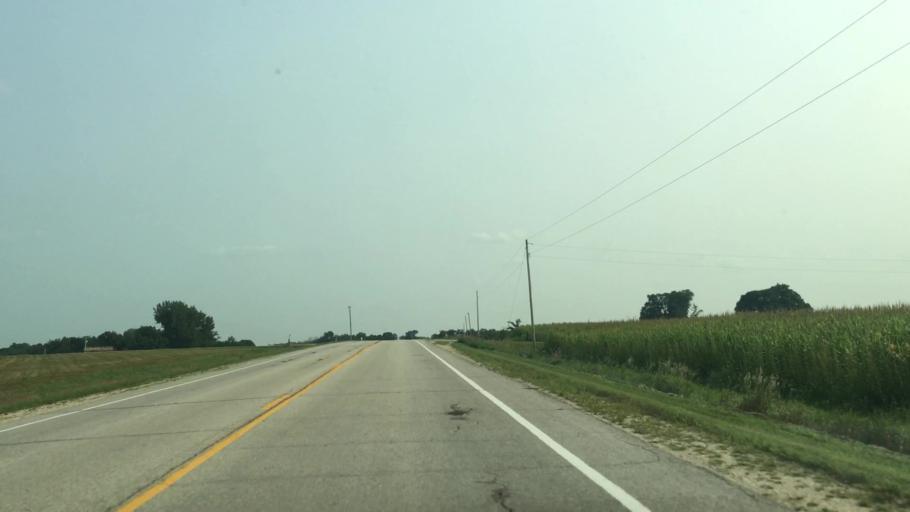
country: US
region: Minnesota
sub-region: Fillmore County
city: Harmony
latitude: 43.6734
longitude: -91.9386
